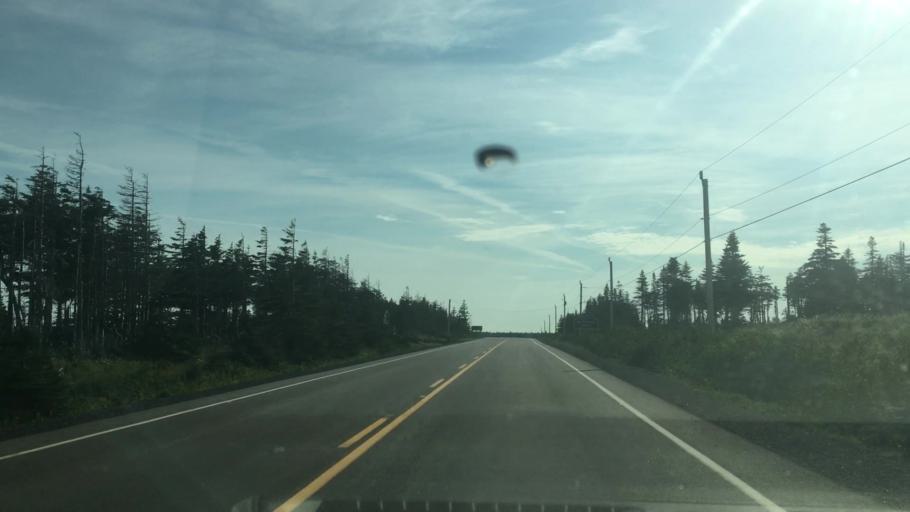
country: CA
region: Nova Scotia
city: Sydney Mines
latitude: 46.8179
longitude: -60.6702
